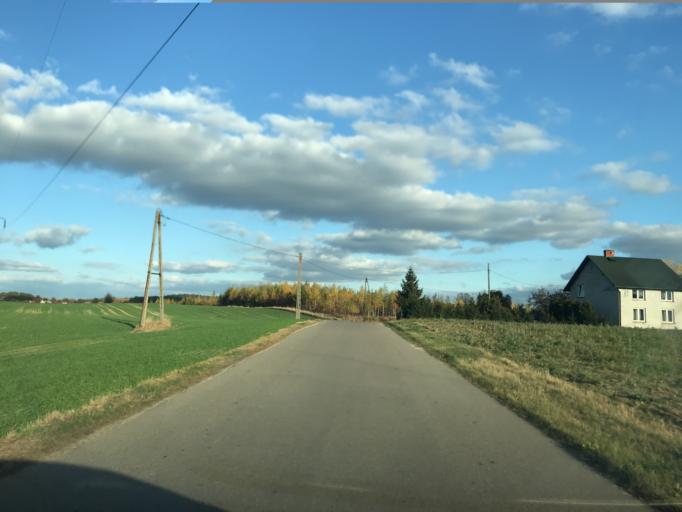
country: PL
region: Warmian-Masurian Voivodeship
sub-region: Powiat dzialdowski
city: Rybno
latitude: 53.3766
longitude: 19.8251
